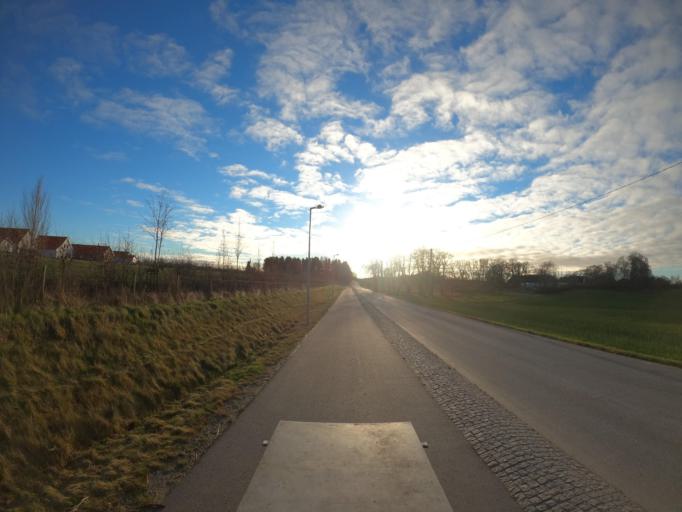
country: SE
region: Skane
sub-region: Svedala Kommun
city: Svedala
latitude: 55.4979
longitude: 13.2380
